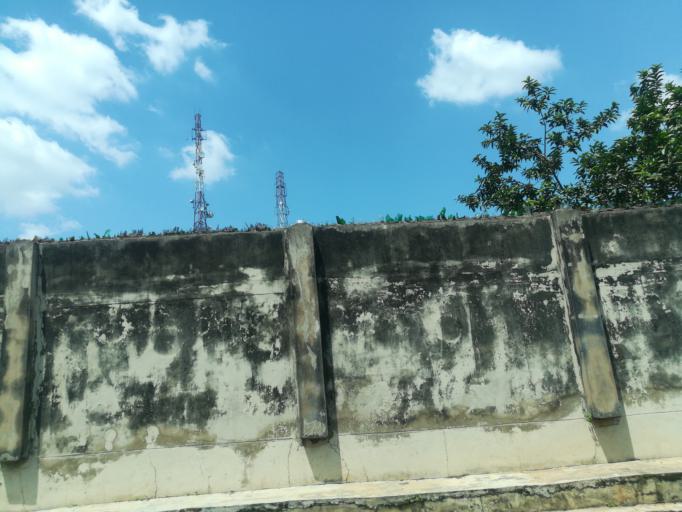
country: NG
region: Oyo
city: Ibadan
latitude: 7.3612
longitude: 3.8709
